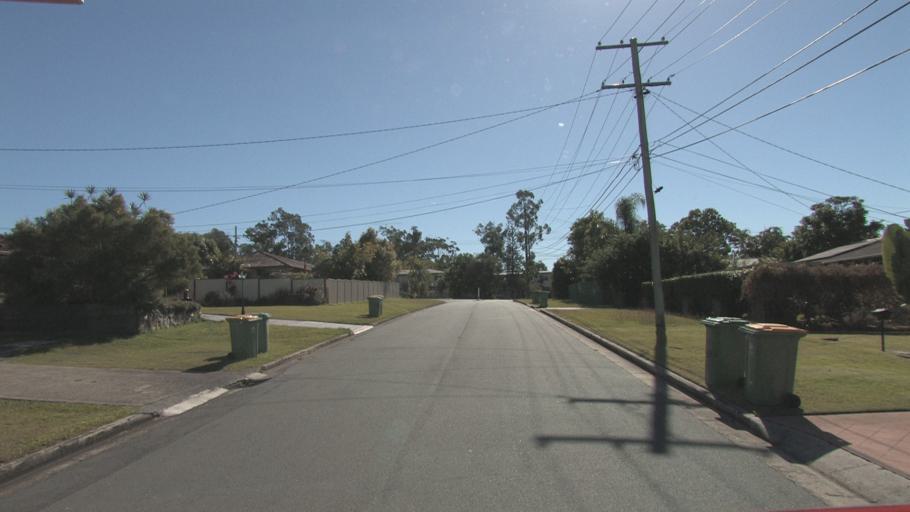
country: AU
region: Queensland
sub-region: Brisbane
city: Sunnybank Hills
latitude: -27.6569
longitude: 153.0503
